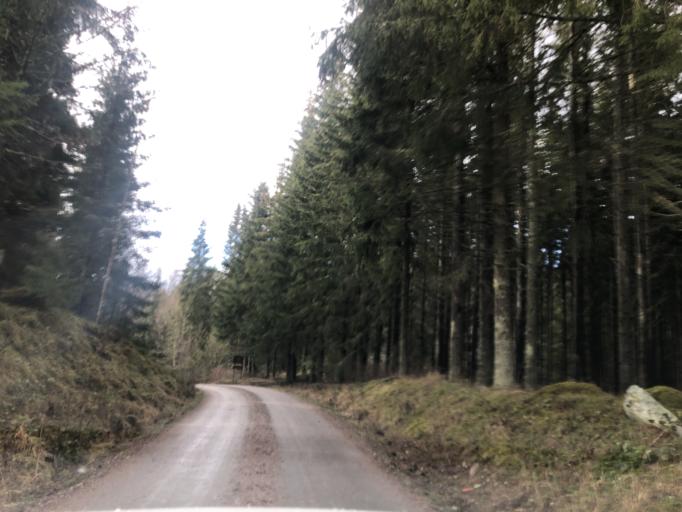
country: SE
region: Vaestra Goetaland
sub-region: Ulricehamns Kommun
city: Ulricehamn
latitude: 57.8285
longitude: 13.2336
